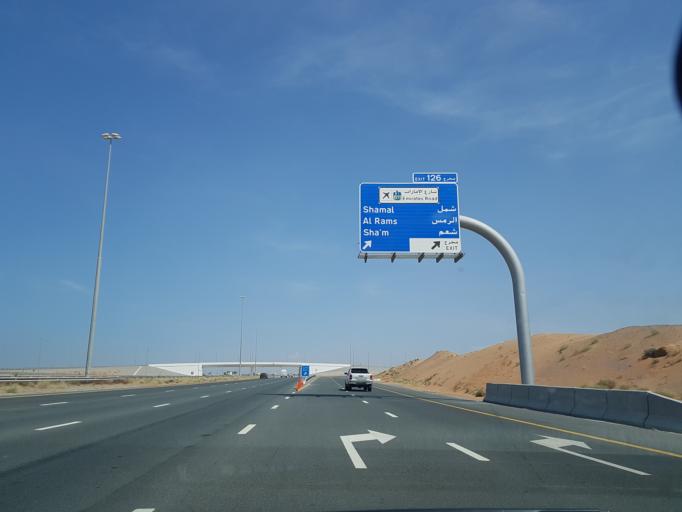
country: AE
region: Ra's al Khaymah
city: Ras al-Khaimah
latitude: 25.6688
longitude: 55.8785
